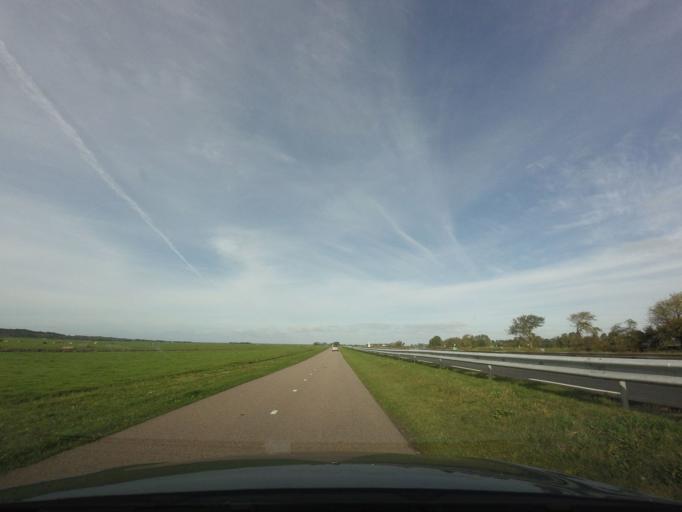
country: NL
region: North Holland
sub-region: Gemeente Schagen
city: Harenkarspel
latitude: 52.7199
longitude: 4.7043
